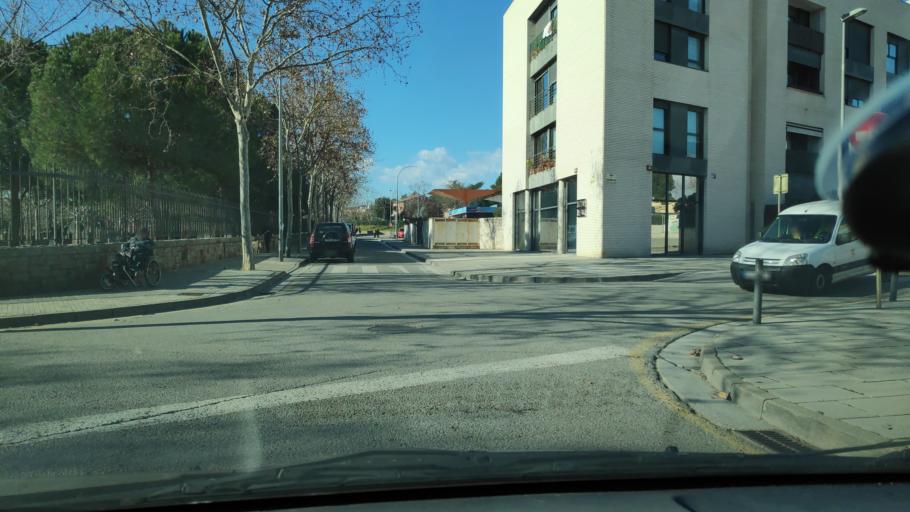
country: ES
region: Catalonia
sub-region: Provincia de Barcelona
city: Sant Quirze del Valles
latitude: 41.5357
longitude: 2.0863
